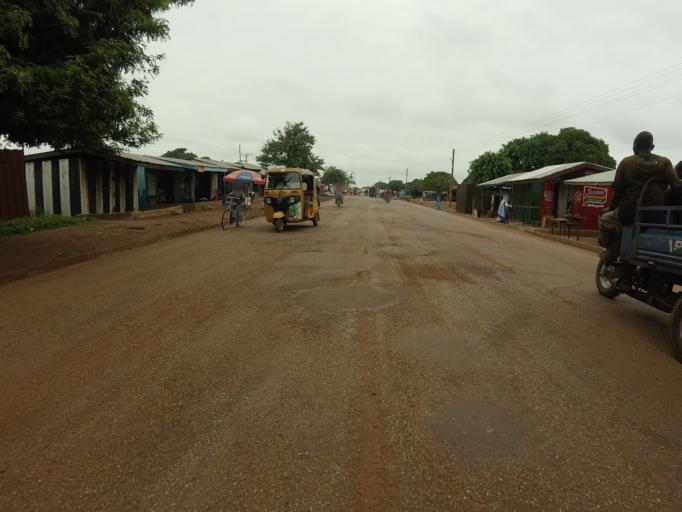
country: GH
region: Northern
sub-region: Yendi
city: Yendi
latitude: 9.4487
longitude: -0.0077
